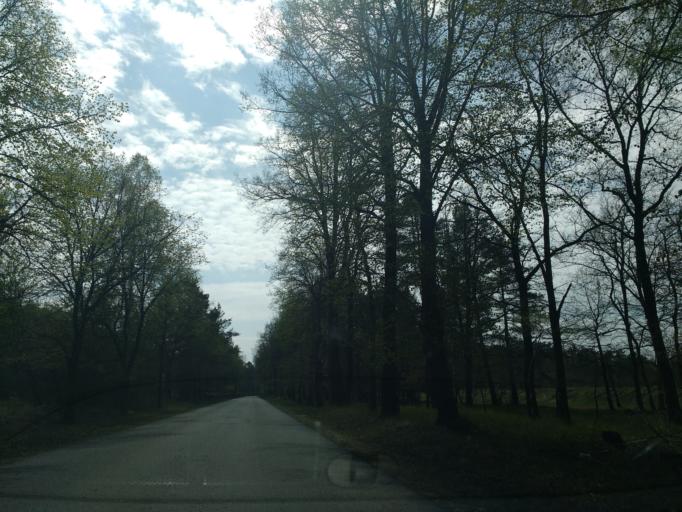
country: DE
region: North Rhine-Westphalia
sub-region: Regierungsbezirk Detmold
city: Hovelhof
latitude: 51.8028
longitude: 8.7222
